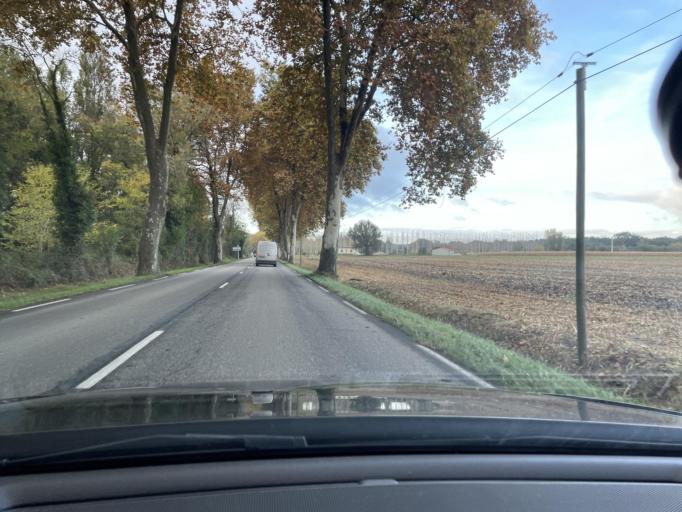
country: FR
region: Aquitaine
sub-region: Departement du Lot-et-Garonne
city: Casteljaloux
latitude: 44.3754
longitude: 0.1057
